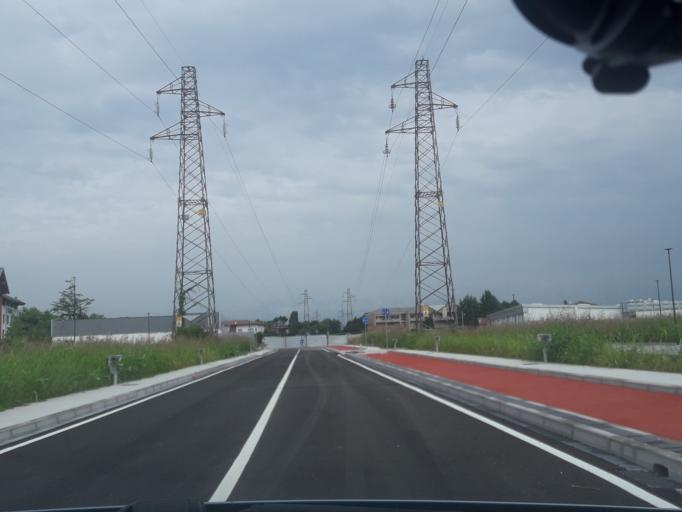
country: IT
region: Friuli Venezia Giulia
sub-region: Provincia di Udine
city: Udine
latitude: 46.0698
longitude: 13.2586
